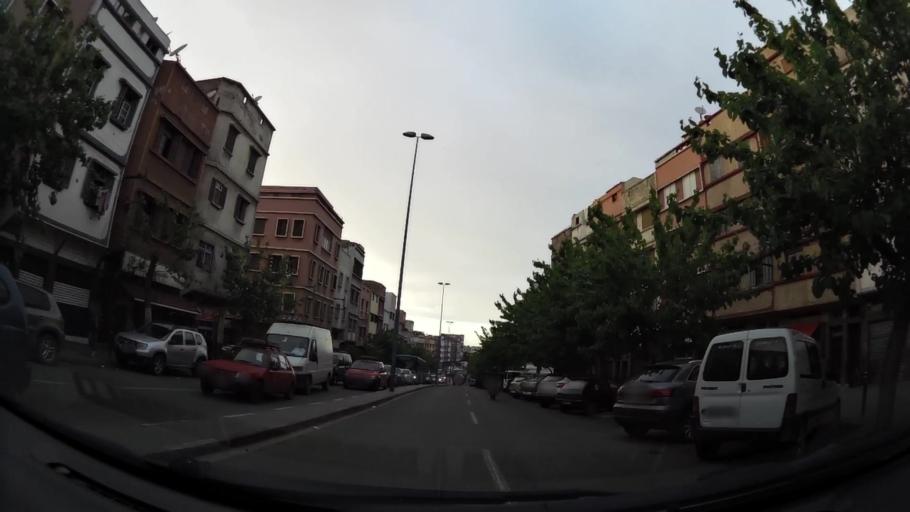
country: MA
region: Grand Casablanca
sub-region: Casablanca
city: Casablanca
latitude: 33.5553
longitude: -7.6002
